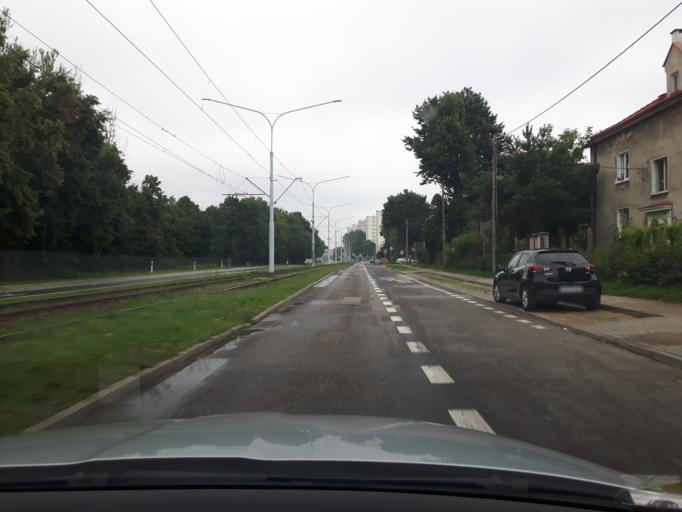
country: PL
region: Pomeranian Voivodeship
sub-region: Sopot
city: Sopot
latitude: 54.4019
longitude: 18.5661
